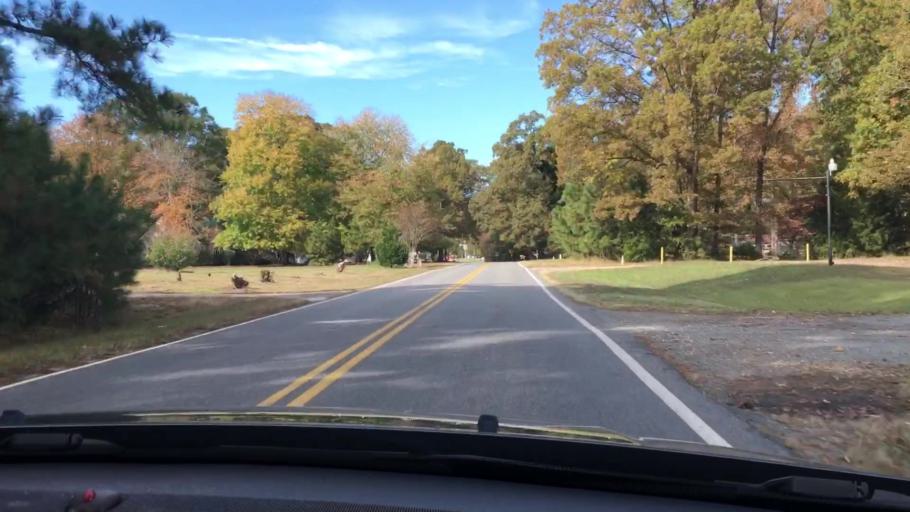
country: US
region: Virginia
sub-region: King William County
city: West Point
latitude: 37.5209
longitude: -76.8238
